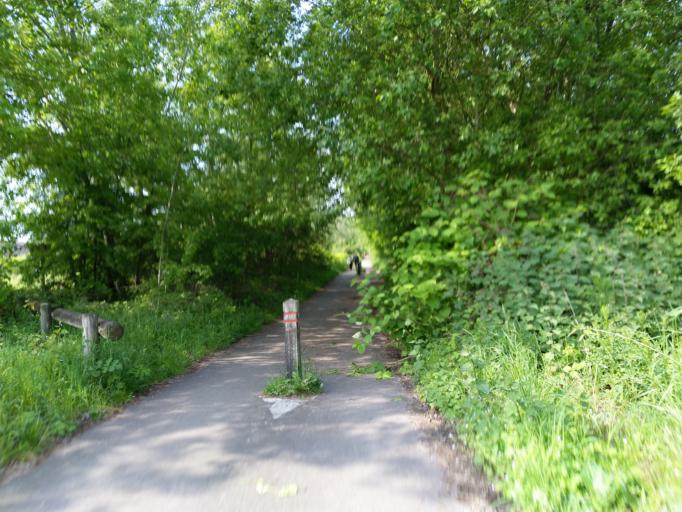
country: BE
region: Wallonia
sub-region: Province du Hainaut
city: Dour
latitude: 50.4048
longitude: 3.7733
